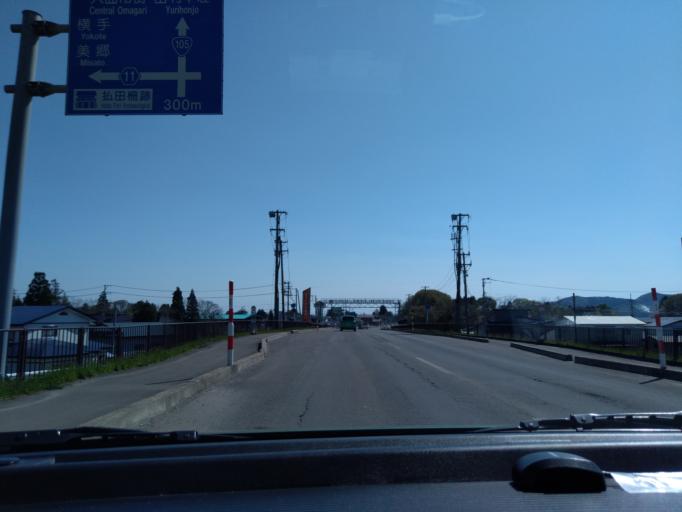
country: JP
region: Akita
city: Kakunodatemachi
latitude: 39.5785
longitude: 140.5669
